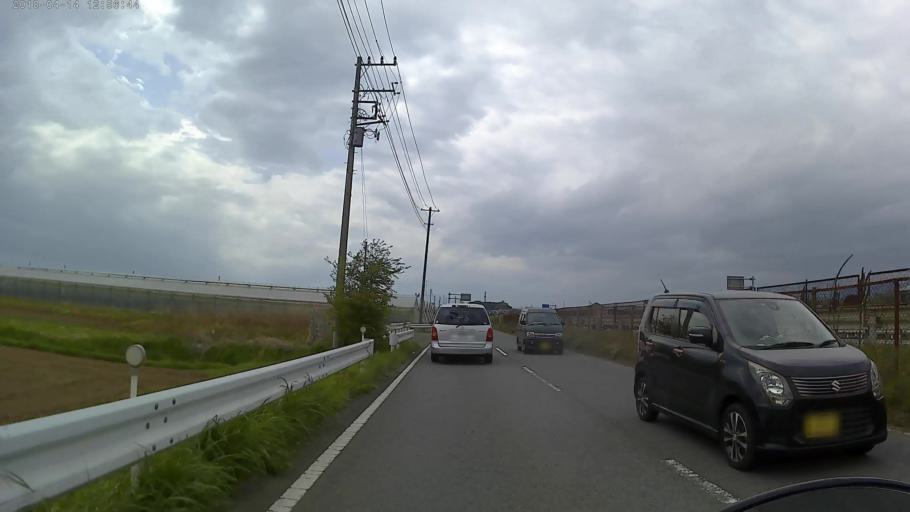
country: JP
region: Kanagawa
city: Isehara
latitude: 35.3748
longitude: 139.3226
